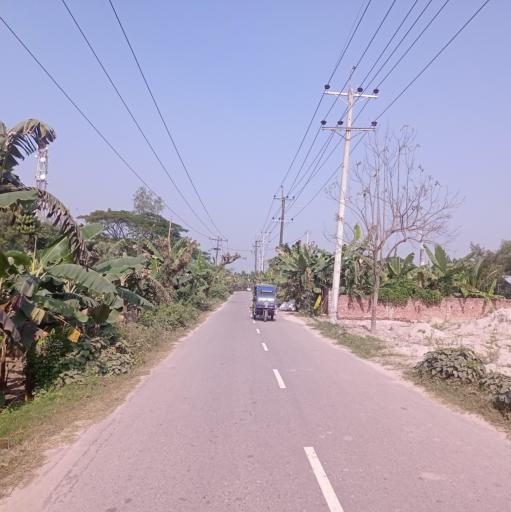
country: BD
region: Dhaka
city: Narsingdi
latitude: 24.0789
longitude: 90.6940
